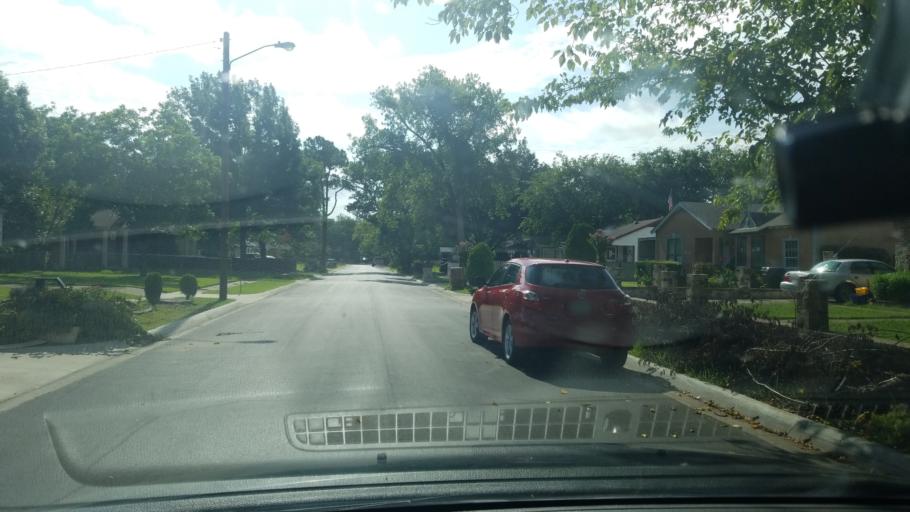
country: US
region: Texas
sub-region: Dallas County
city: Balch Springs
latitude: 32.7413
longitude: -96.6732
